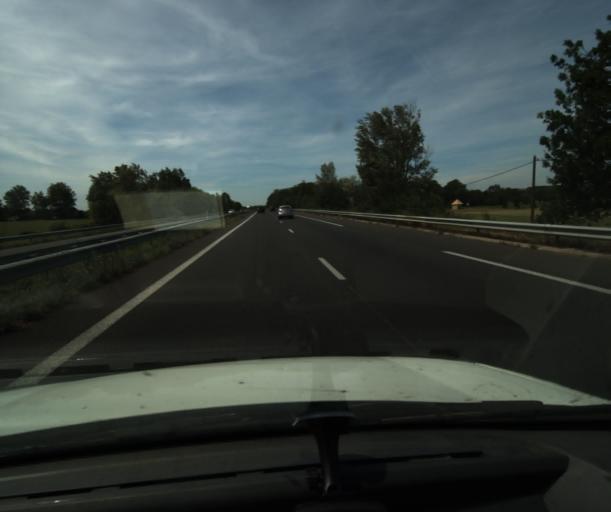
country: FR
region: Languedoc-Roussillon
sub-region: Departement de l'Aude
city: Villeneuve-la-Comptal
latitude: 43.3009
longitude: 1.9219
